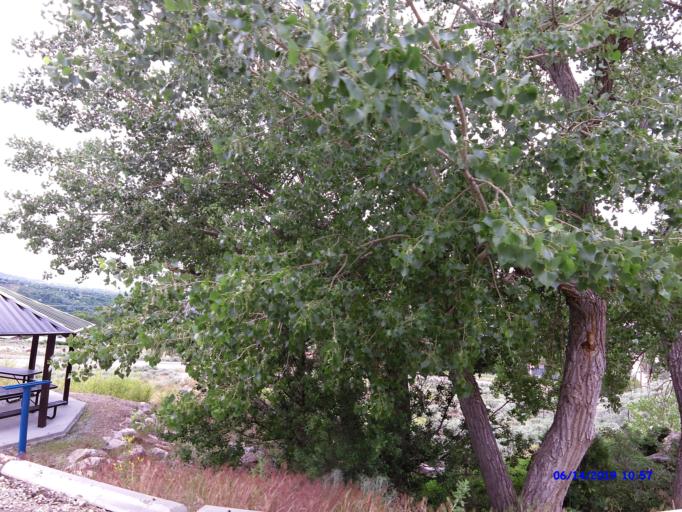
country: US
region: Utah
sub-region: Weber County
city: Ogden
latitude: 41.2482
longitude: -111.9332
